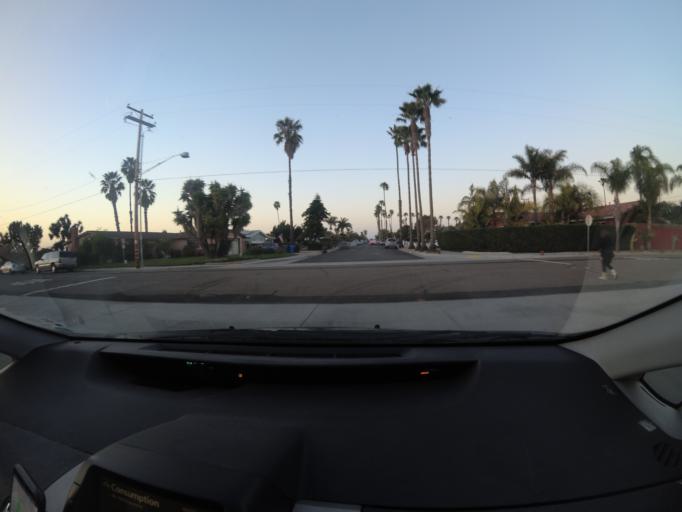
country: US
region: California
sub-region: San Diego County
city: Imperial Beach
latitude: 32.5708
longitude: -117.1226
